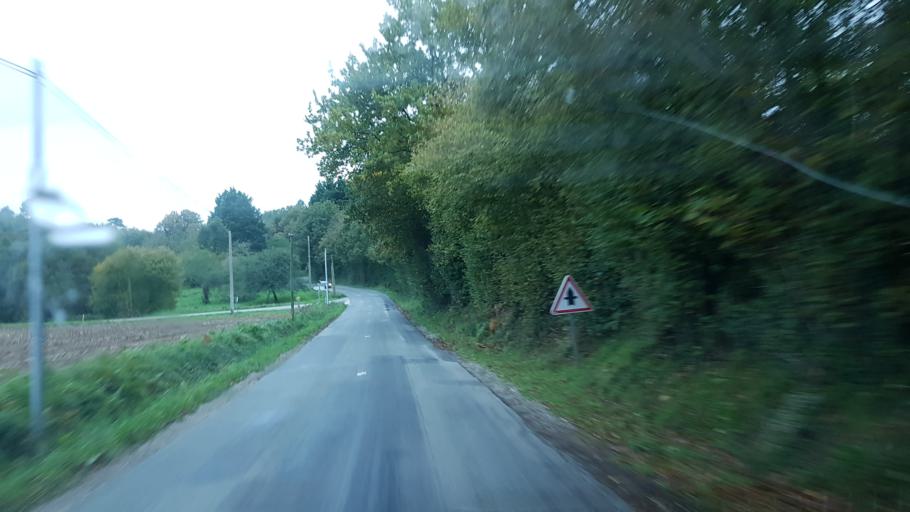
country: FR
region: Brittany
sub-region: Departement du Morbihan
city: Trefflean
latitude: 47.6708
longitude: -2.6147
